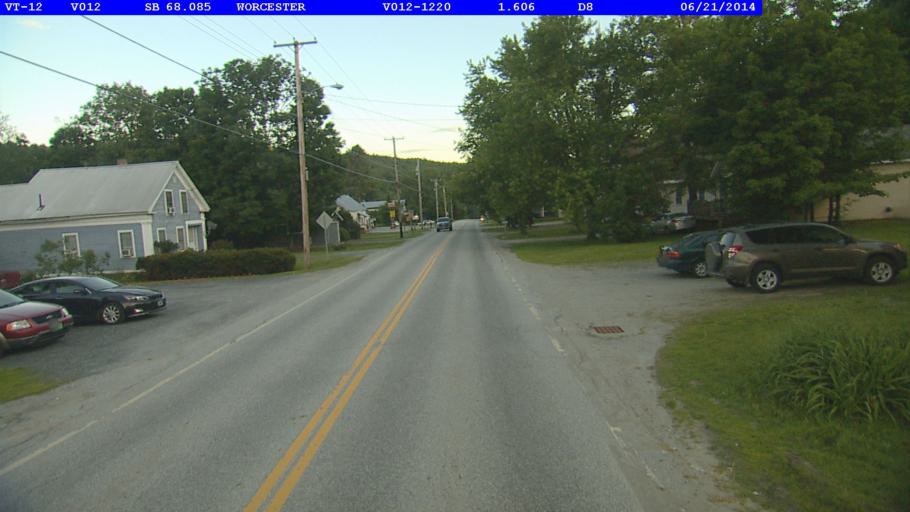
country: US
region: Vermont
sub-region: Washington County
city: Montpelier
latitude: 44.3722
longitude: -72.5505
